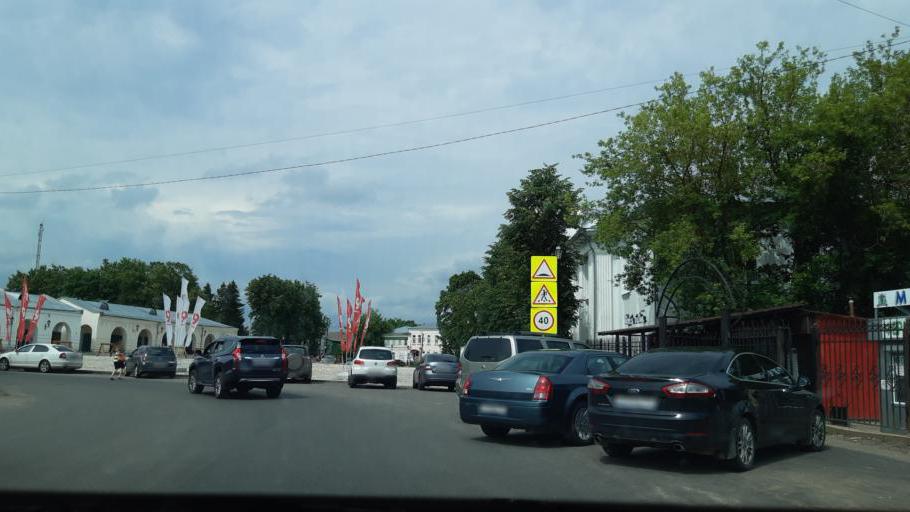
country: RU
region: Moskovskaya
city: Vereya
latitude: 55.3426
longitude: 36.1854
